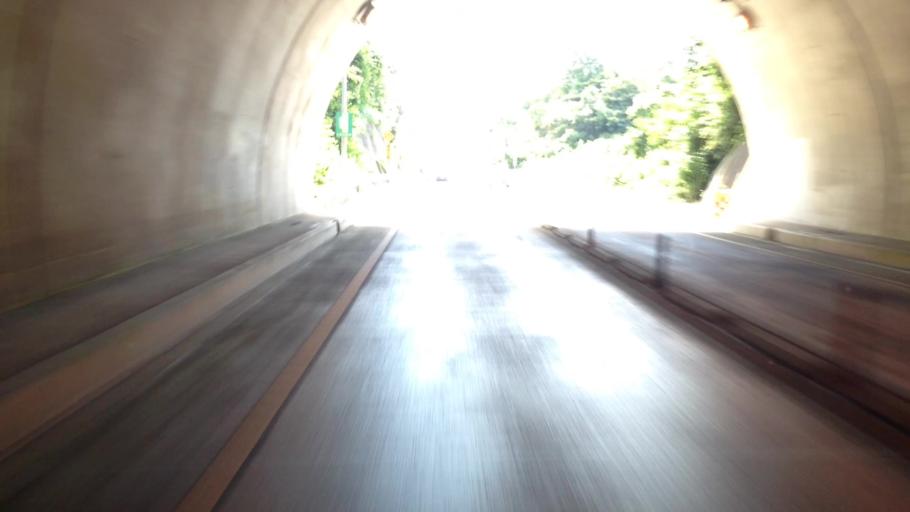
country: JP
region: Kanagawa
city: Yokosuka
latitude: 35.2371
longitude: 139.6518
